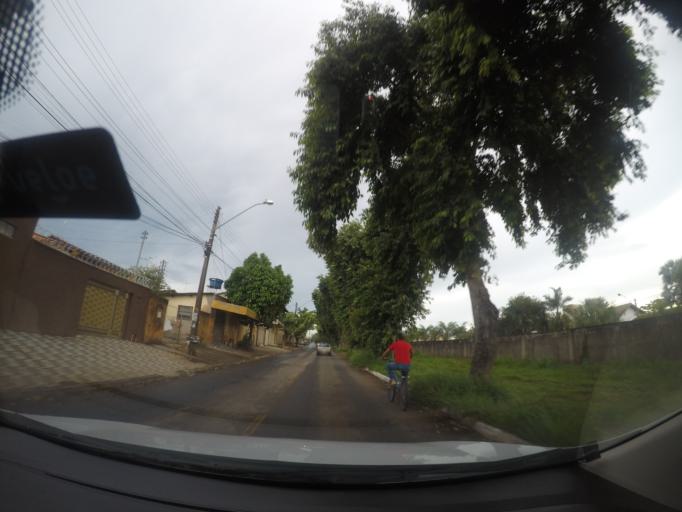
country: BR
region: Goias
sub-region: Goiania
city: Goiania
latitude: -16.7231
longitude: -49.3101
